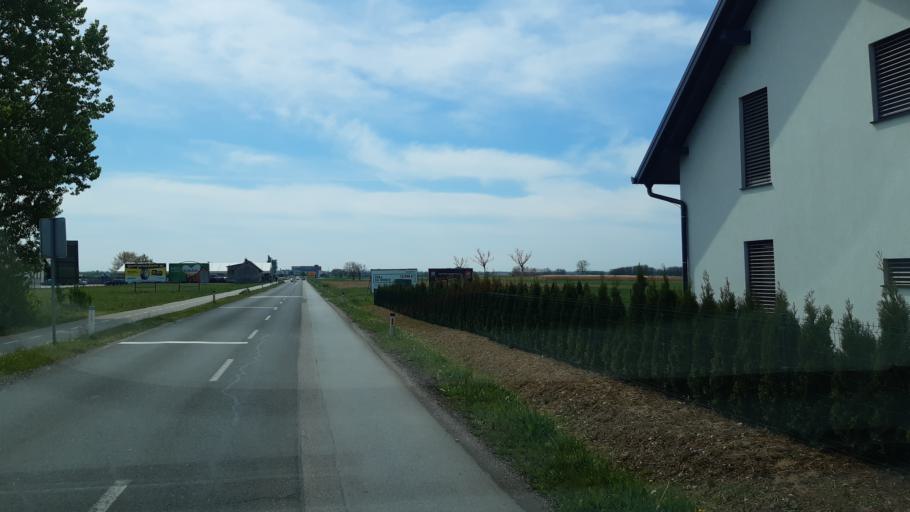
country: SI
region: Murska Sobota
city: Murska Sobota
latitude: 46.6530
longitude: 16.1694
